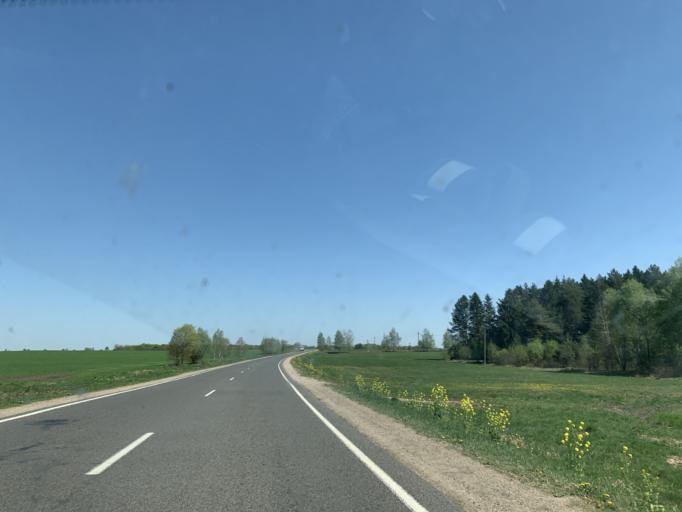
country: BY
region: Minsk
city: Kapyl'
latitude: 53.2567
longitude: 26.9333
